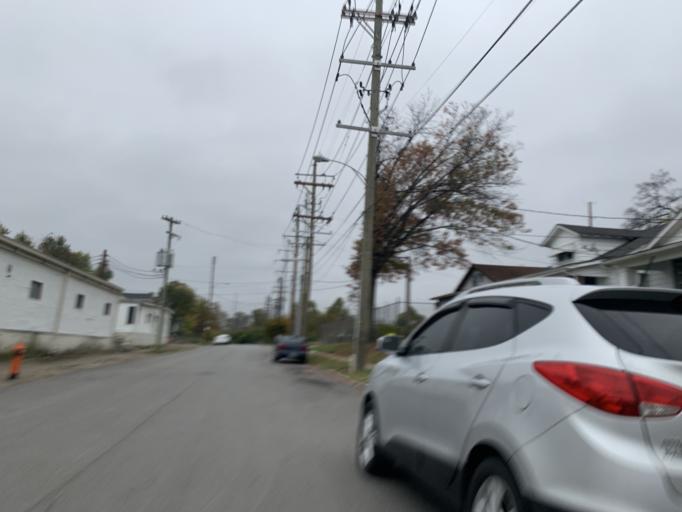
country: US
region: Indiana
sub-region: Floyd County
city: New Albany
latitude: 38.2527
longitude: -85.8040
